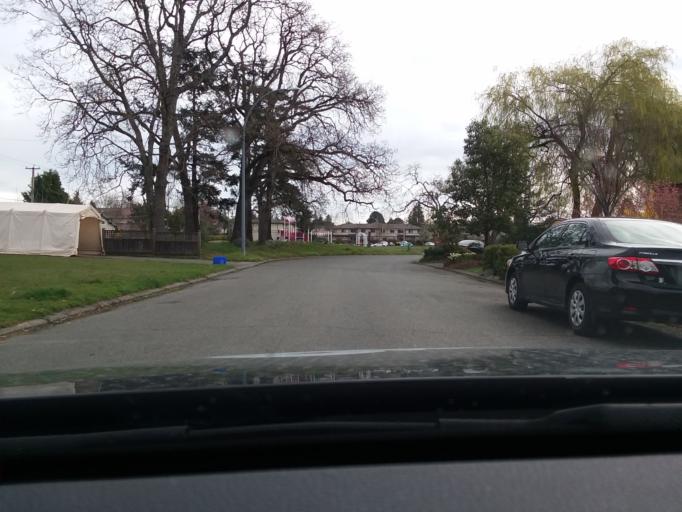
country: CA
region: British Columbia
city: Oak Bay
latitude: 48.4743
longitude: -123.3280
